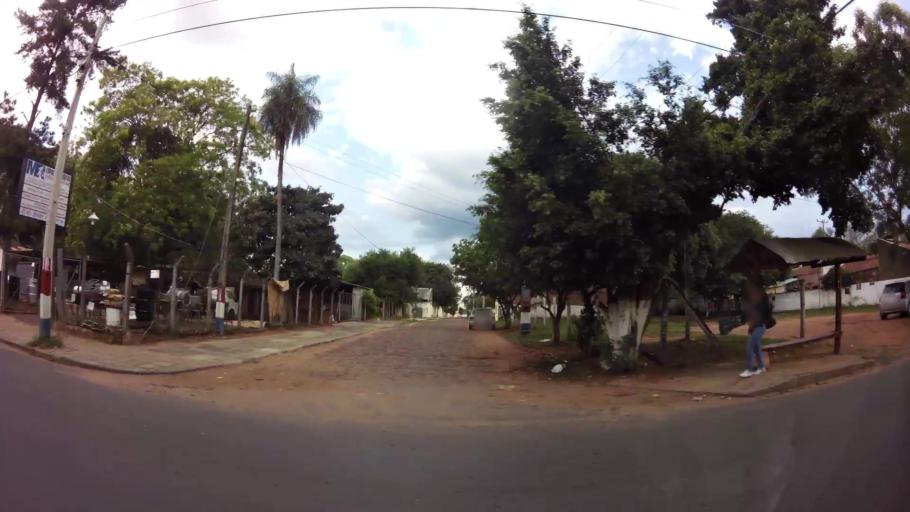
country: PY
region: Central
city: Fernando de la Mora
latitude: -25.3388
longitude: -57.5444
